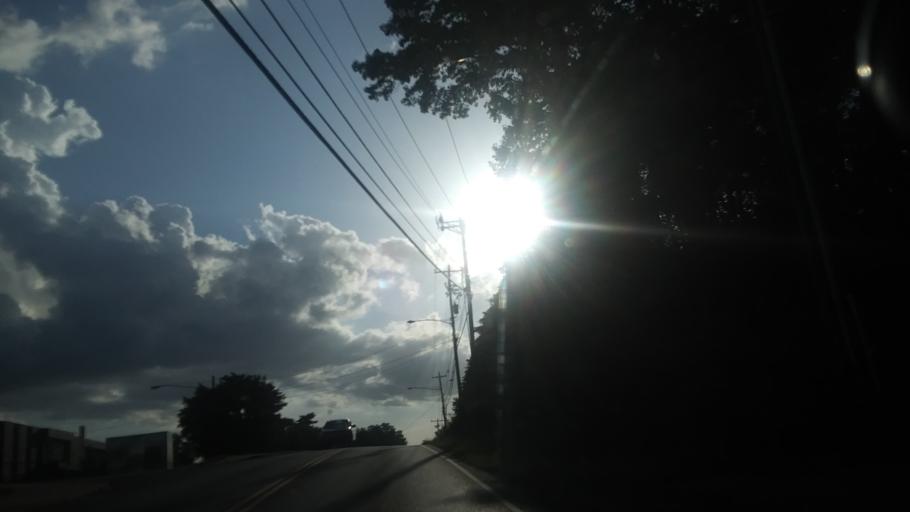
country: US
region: Tennessee
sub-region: Rutherford County
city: La Vergne
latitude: 36.0674
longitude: -86.6632
